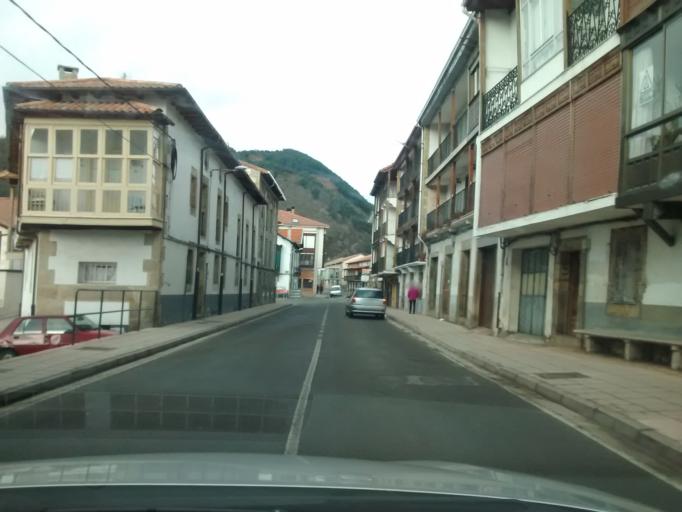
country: ES
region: Castille and Leon
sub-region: Provincia de Burgos
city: Espinosa de los Monteros
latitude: 43.0785
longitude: -3.5528
